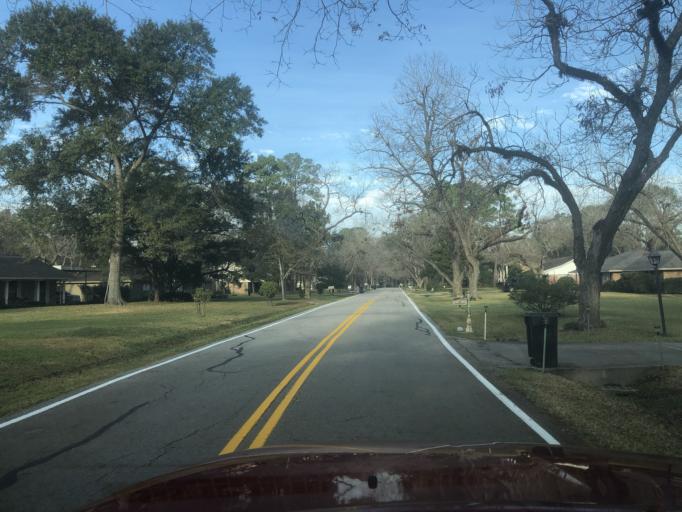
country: US
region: Texas
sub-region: Harris County
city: Spring
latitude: 30.0113
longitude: -95.4730
